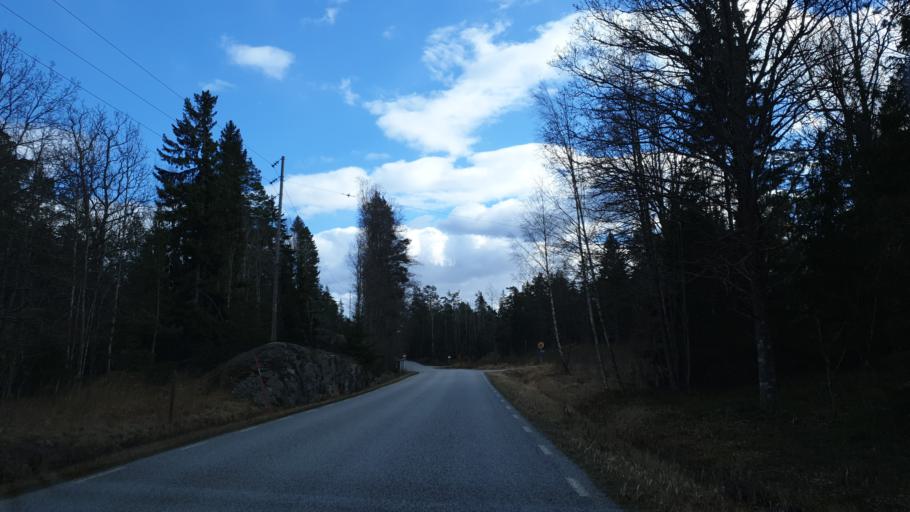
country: SE
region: Stockholm
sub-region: Varmdo Kommun
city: Hemmesta
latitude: 59.2325
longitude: 18.4822
